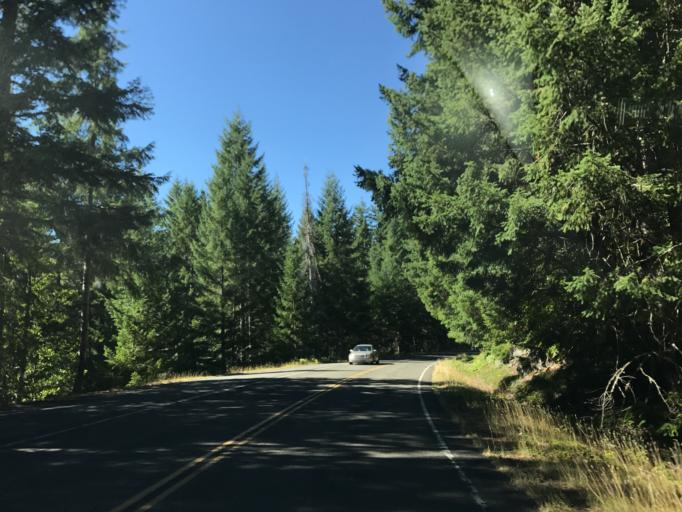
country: US
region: Washington
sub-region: Pierce County
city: Buckley
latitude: 46.7432
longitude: -121.6187
